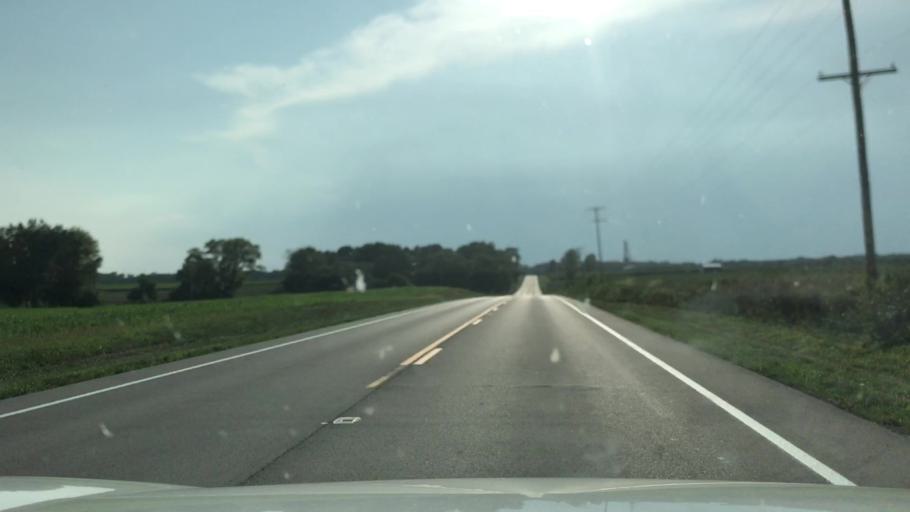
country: US
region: Illinois
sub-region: Washington County
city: Nashville
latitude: 38.4415
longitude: -89.3937
